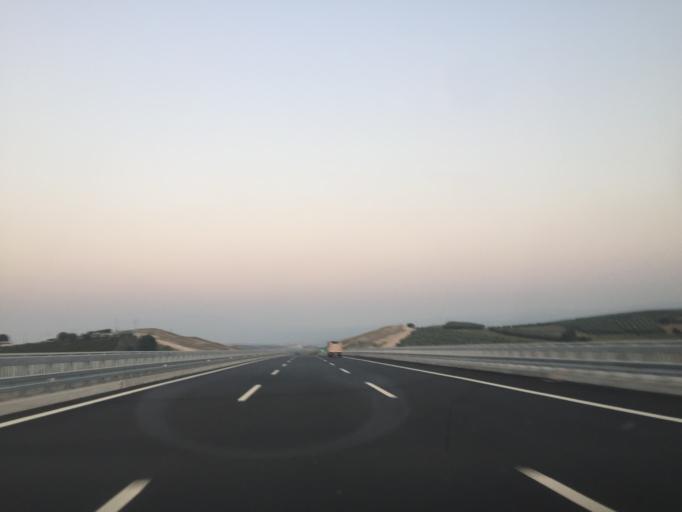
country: TR
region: Bursa
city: Gorukle
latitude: 40.2495
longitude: 28.7503
